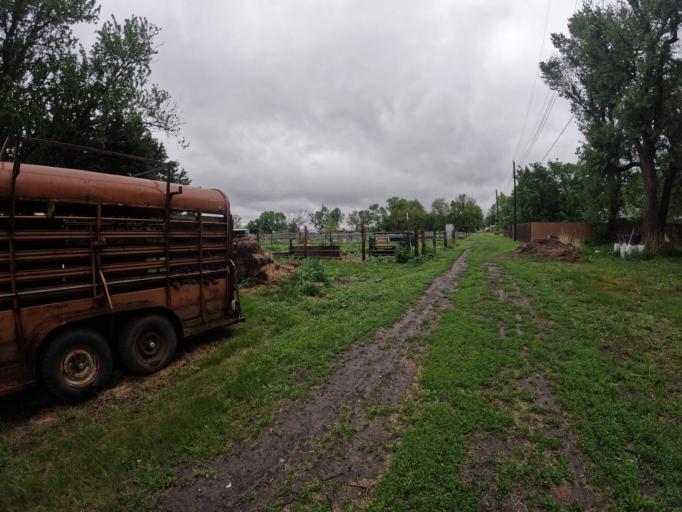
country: US
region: Nebraska
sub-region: Clay County
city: Harvard
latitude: 40.6230
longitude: -98.0992
